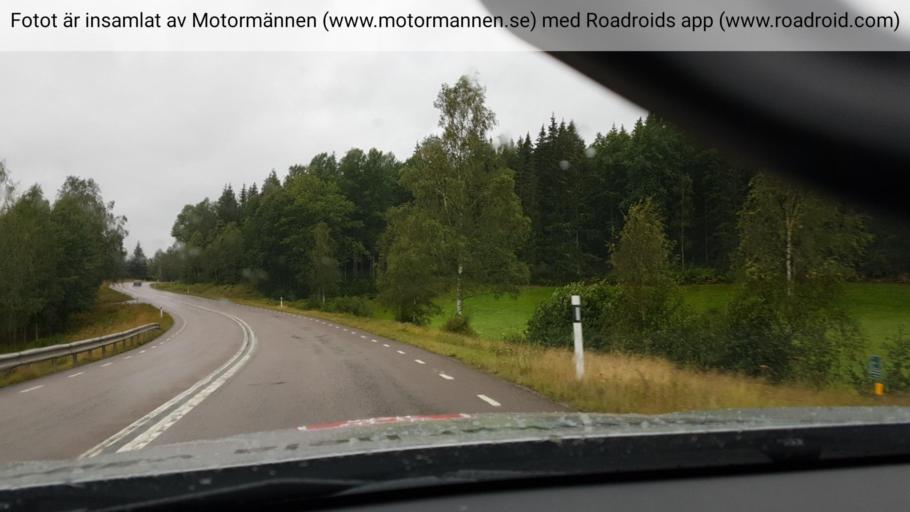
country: SE
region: Vaestra Goetaland
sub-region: Dals-Ed Kommun
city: Ed
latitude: 58.9246
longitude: 12.0326
